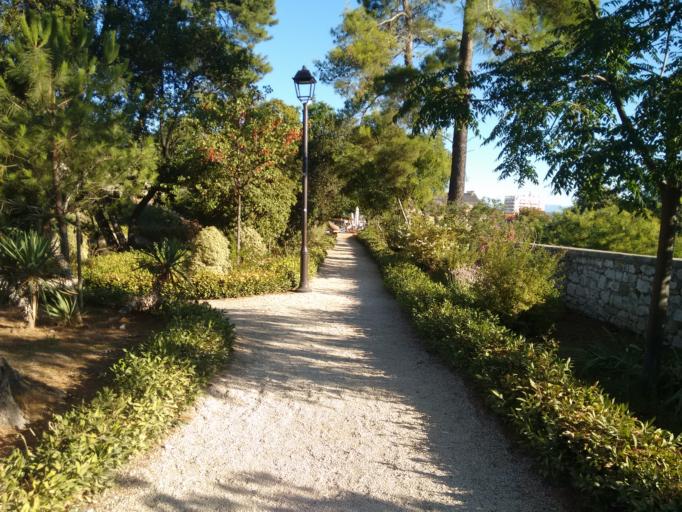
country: HR
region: Zadarska
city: Zadar
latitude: 44.1120
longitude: 15.2301
